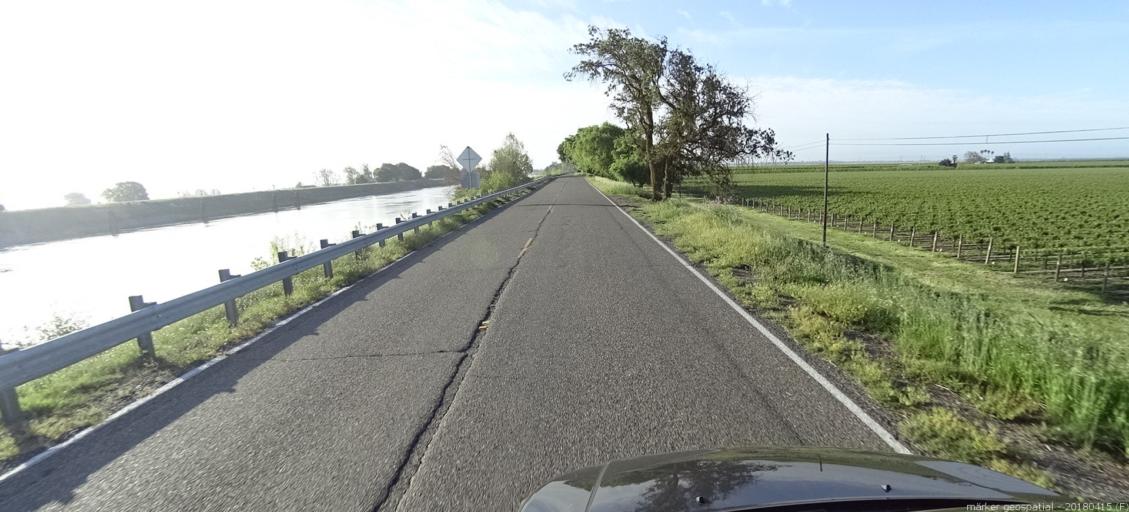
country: US
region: California
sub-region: Sacramento County
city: Walnut Grove
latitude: 38.3011
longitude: -121.5713
